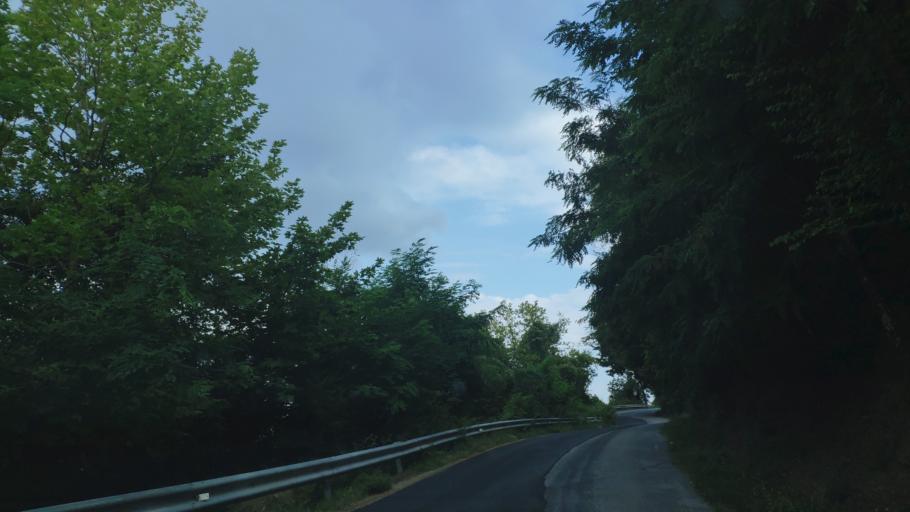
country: GR
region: Epirus
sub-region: Nomos Artas
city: Agios Dimitrios
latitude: 39.3881
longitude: 21.0232
